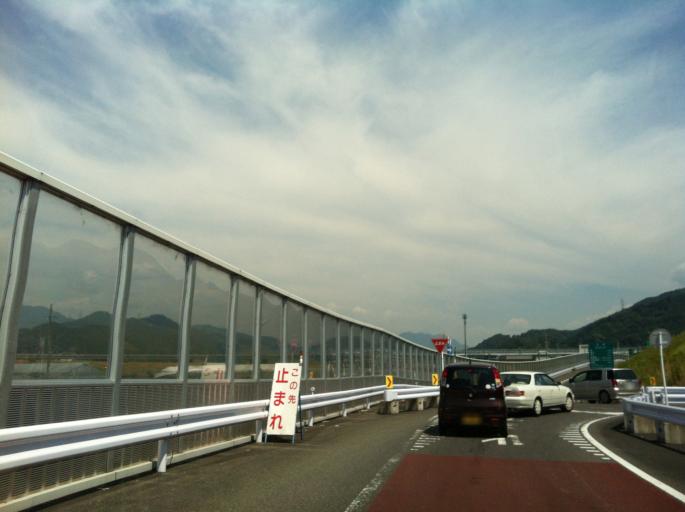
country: JP
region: Shizuoka
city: Shizuoka-shi
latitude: 35.0350
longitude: 138.3776
